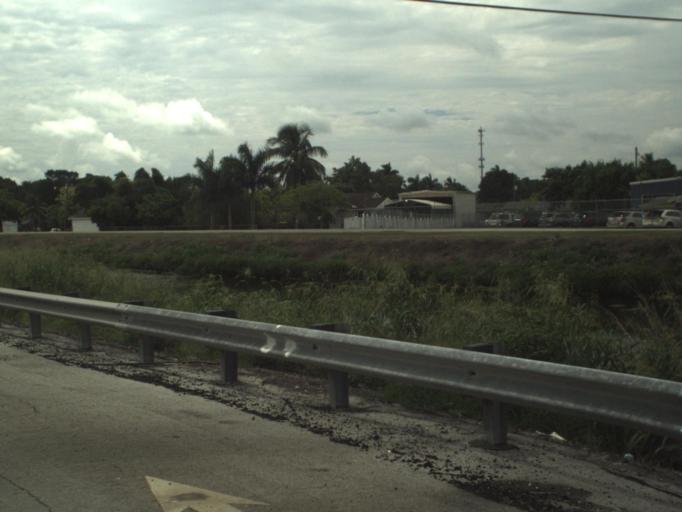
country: US
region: Florida
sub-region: Palm Beach County
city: Belle Glade
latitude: 26.6941
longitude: -80.6837
